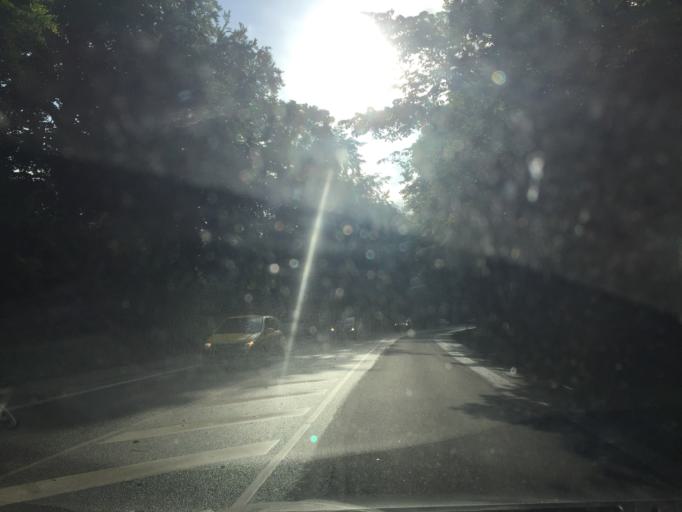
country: DK
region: Zealand
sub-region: Slagelse Kommune
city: Slagelse
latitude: 55.3921
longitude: 11.3642
